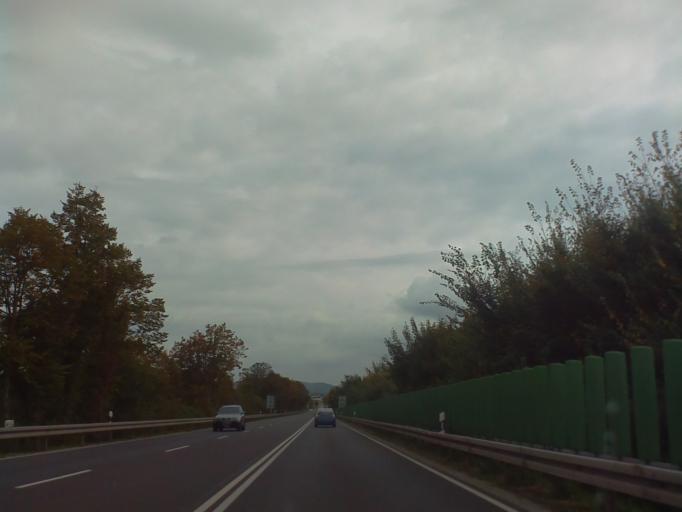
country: DE
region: Hesse
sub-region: Regierungsbezirk Kassel
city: Burghaun
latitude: 50.6986
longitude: 9.7342
